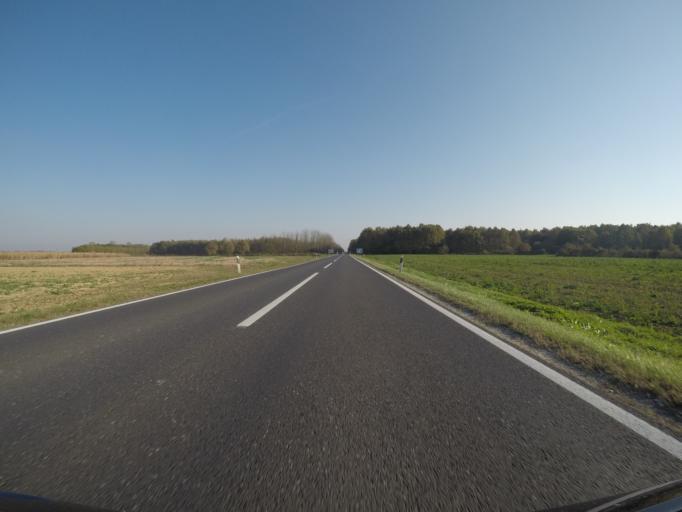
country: HR
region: Koprivnicko-Krizevacka
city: Kalinovac
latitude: 46.0005
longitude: 17.1159
